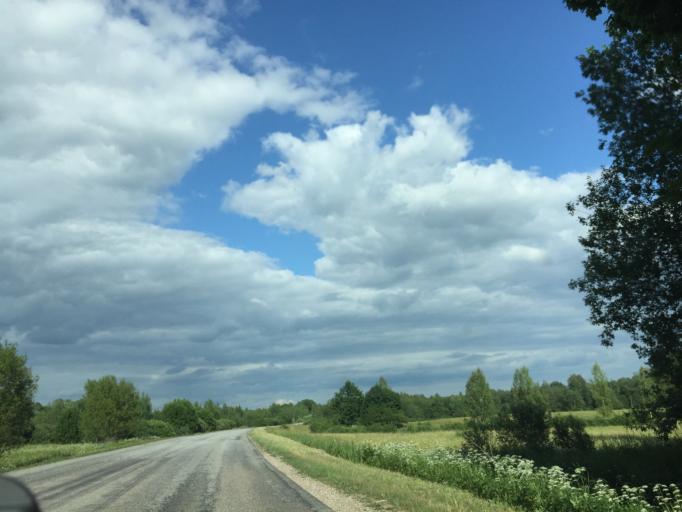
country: LV
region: Ogre
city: Jumprava
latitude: 56.7989
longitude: 25.0515
